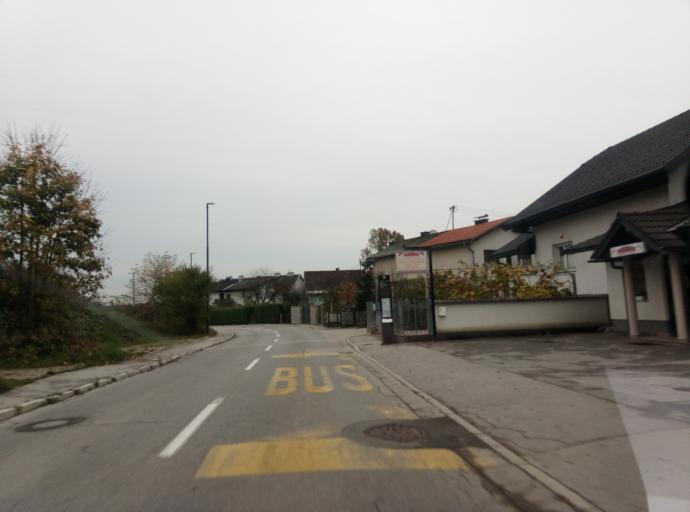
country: SI
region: Trzin
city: Trzin
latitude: 46.1077
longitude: 14.5330
